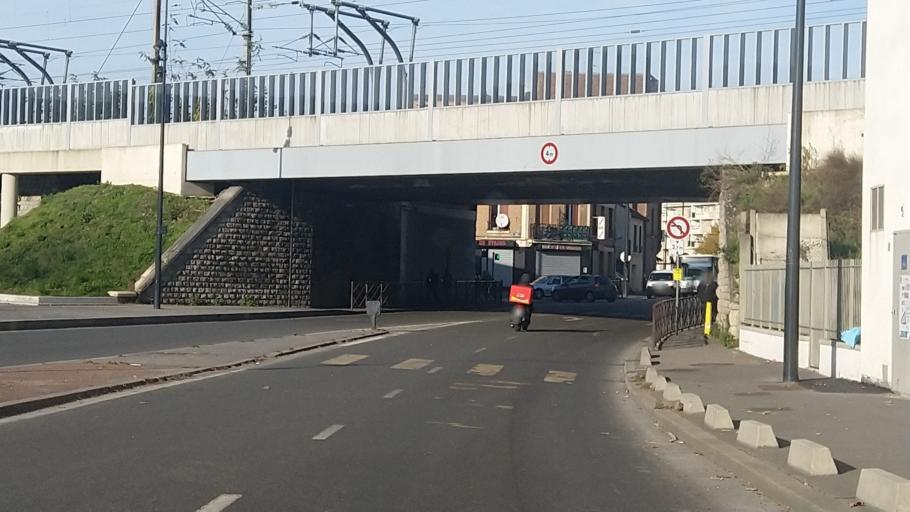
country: FR
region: Ile-de-France
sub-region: Departement de Seine-Saint-Denis
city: Stains
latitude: 48.9580
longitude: 2.3824
